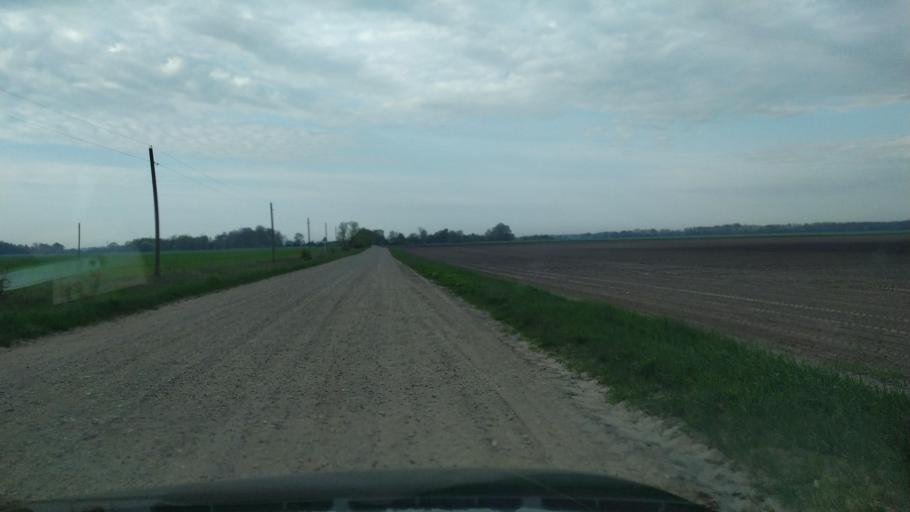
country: BY
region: Brest
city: Zhabinka
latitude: 52.1349
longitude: 24.0930
